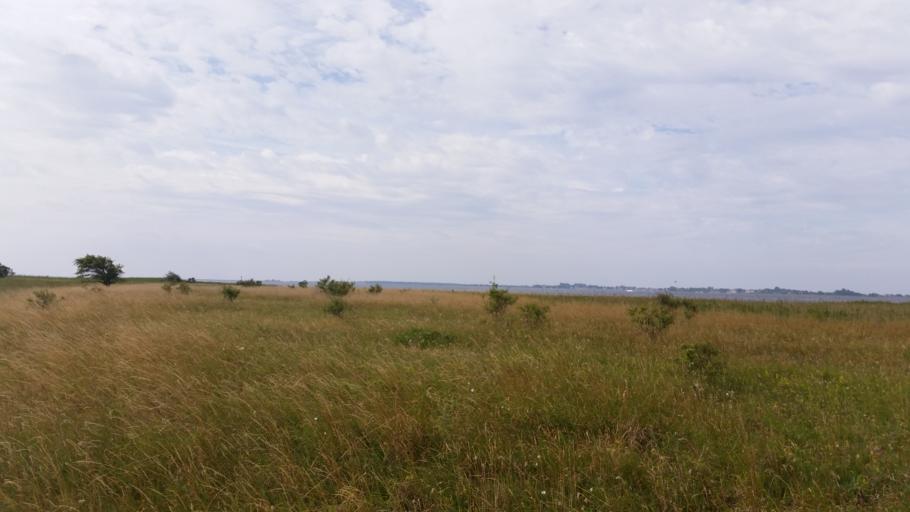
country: DE
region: Mecklenburg-Vorpommern
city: Hiddensee
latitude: 54.5851
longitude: 13.1426
